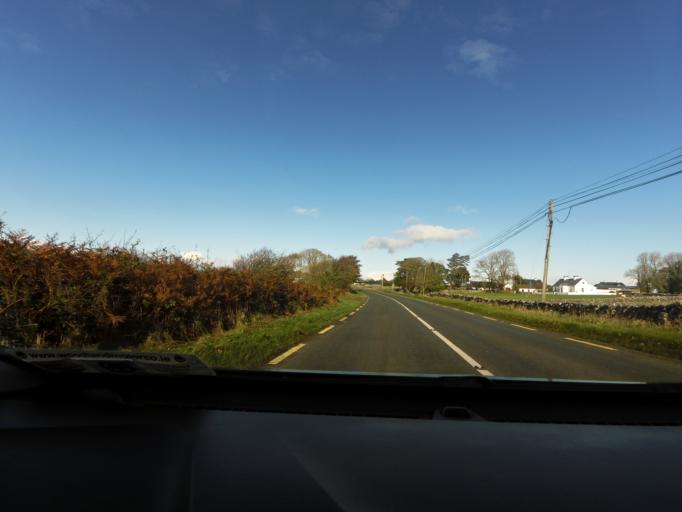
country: IE
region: Connaught
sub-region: Maigh Eo
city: Ballinrobe
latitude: 53.5392
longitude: -9.0951
